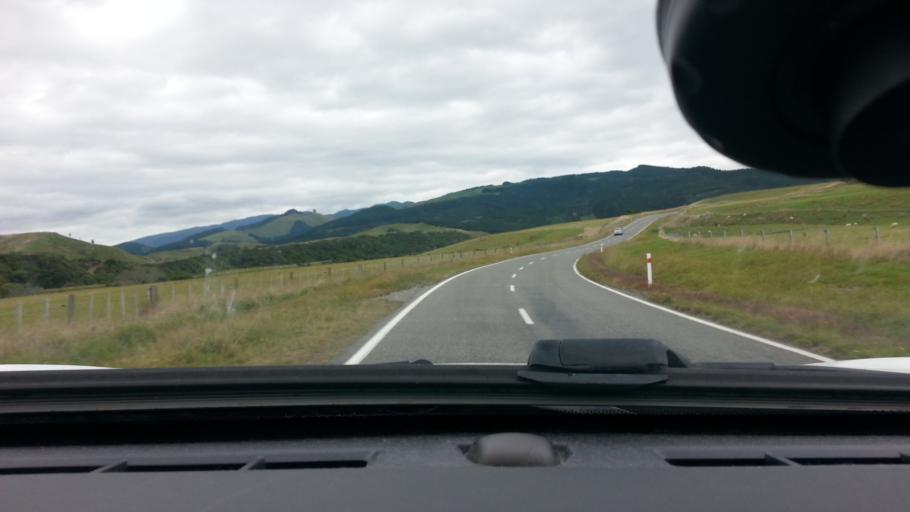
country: NZ
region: Wellington
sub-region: South Wairarapa District
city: Waipawa
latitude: -41.4146
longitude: 175.2073
